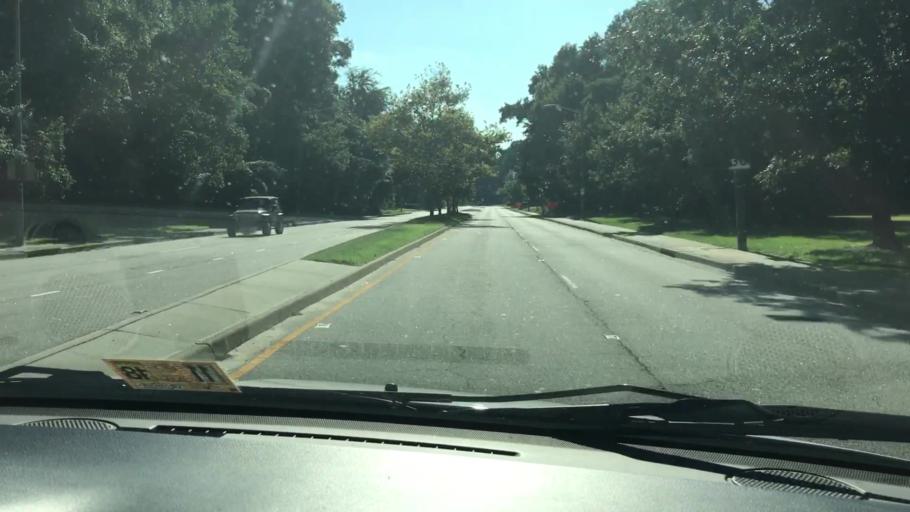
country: US
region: Virginia
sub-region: City of Norfolk
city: Norfolk
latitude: 36.8975
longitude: -76.2163
